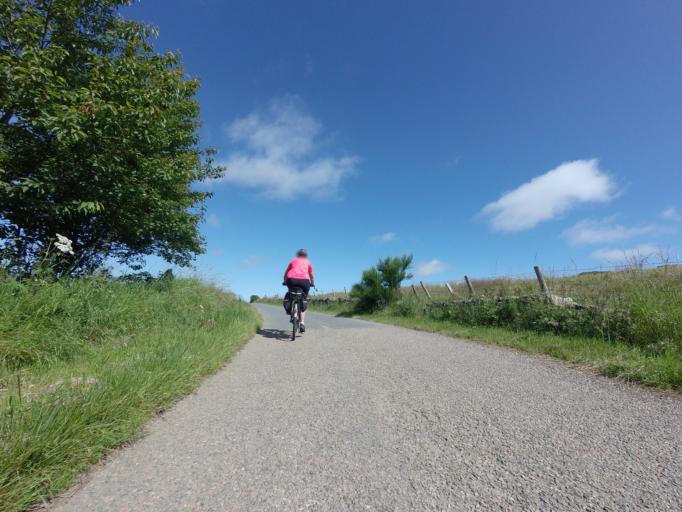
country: GB
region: Scotland
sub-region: Aberdeenshire
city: Banff
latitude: 57.6006
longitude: -2.5115
